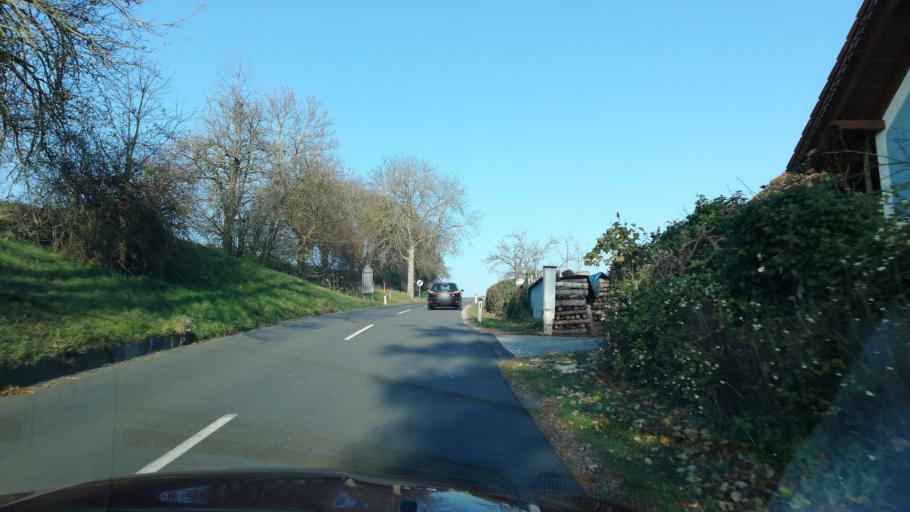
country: AT
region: Upper Austria
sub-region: Wels-Land
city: Buchkirchen
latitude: 48.2401
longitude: 14.0212
